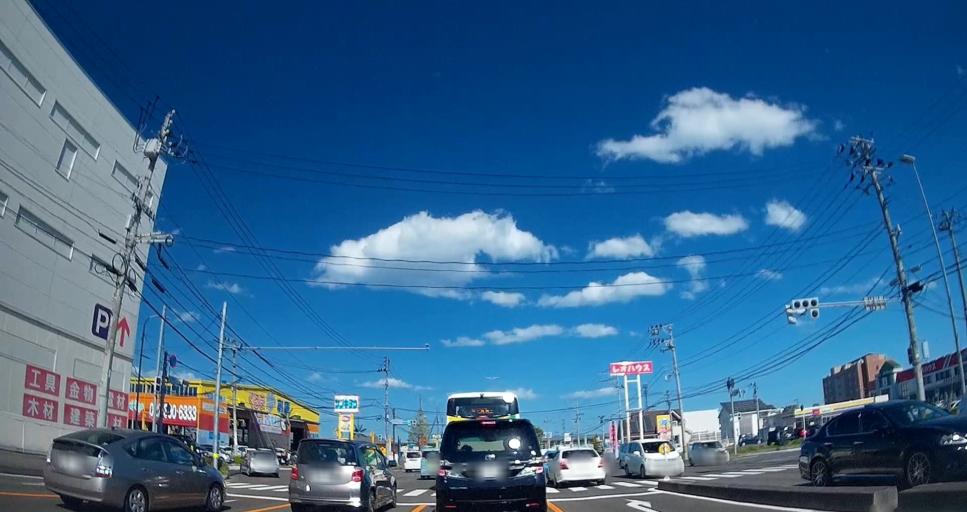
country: JP
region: Miyagi
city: Sendai-shi
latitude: 38.2504
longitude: 140.9518
